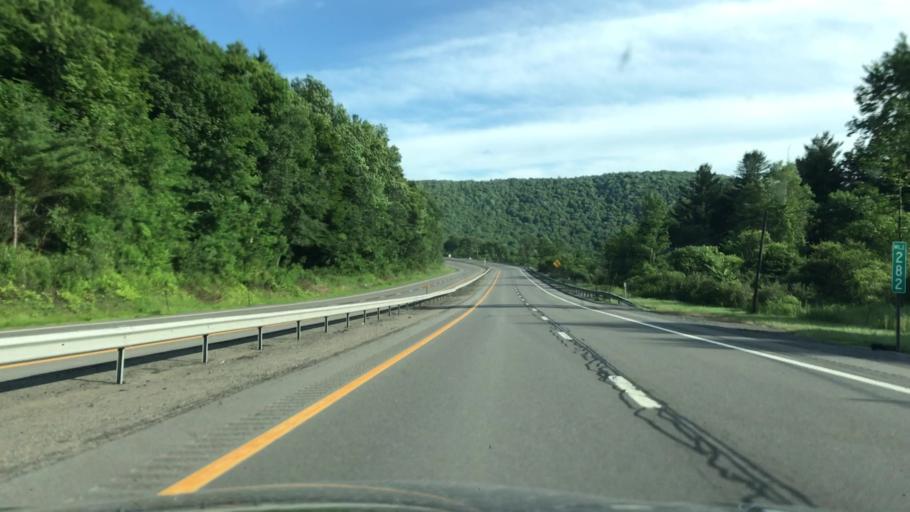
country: US
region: New York
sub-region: Delaware County
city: Hancock
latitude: 41.9766
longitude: -75.3380
